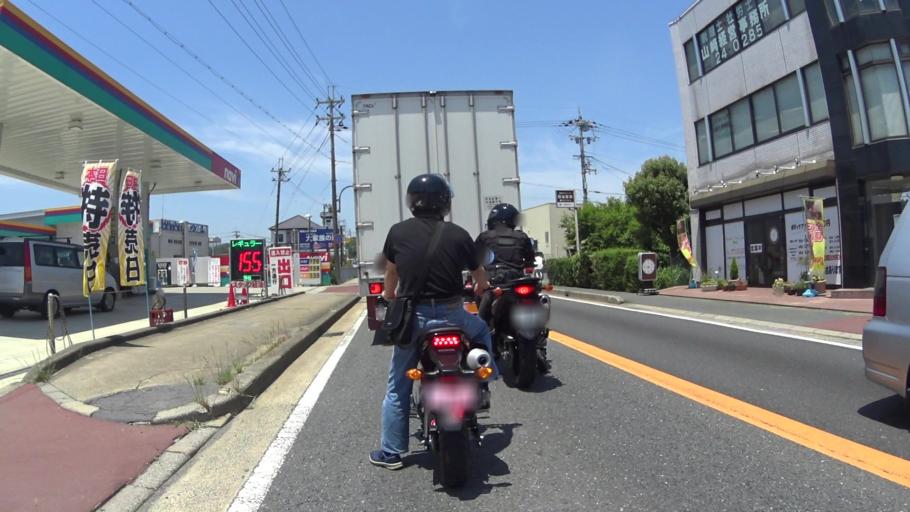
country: JP
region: Kyoto
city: Kameoka
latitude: 35.1231
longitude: 135.4459
